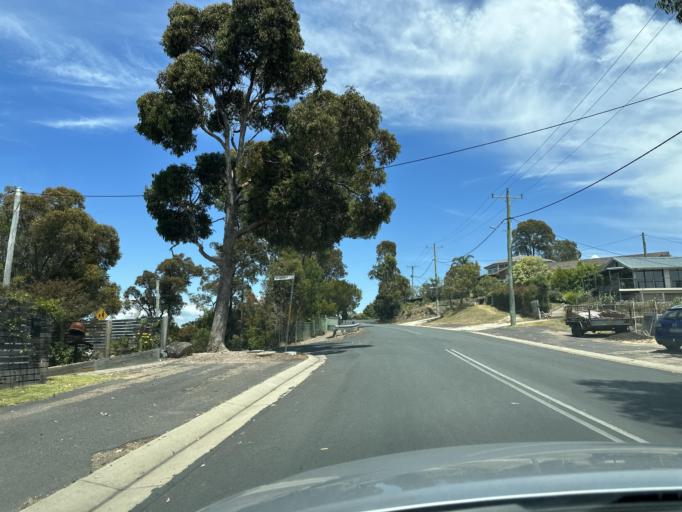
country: AU
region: New South Wales
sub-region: Bega Valley
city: Merimbula
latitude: -36.8915
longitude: 149.9015
